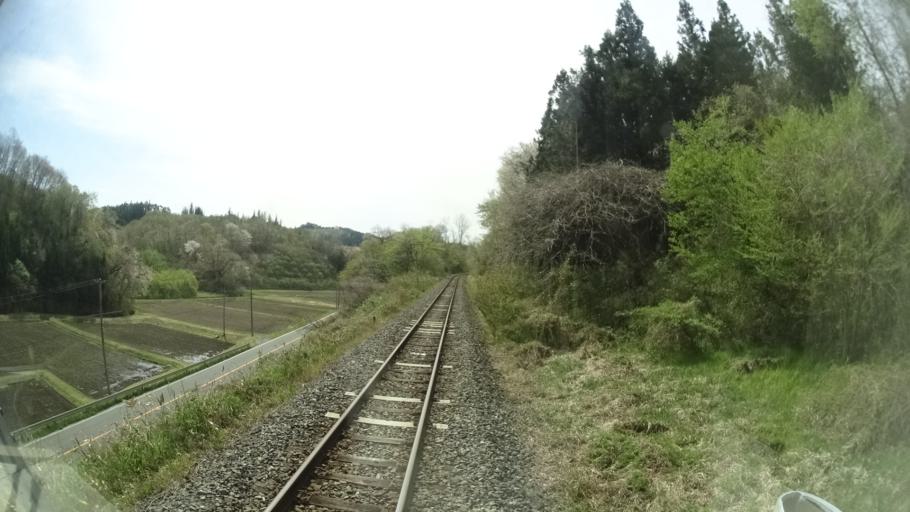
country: JP
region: Iwate
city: Ichinoseki
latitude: 38.9861
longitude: 141.3316
